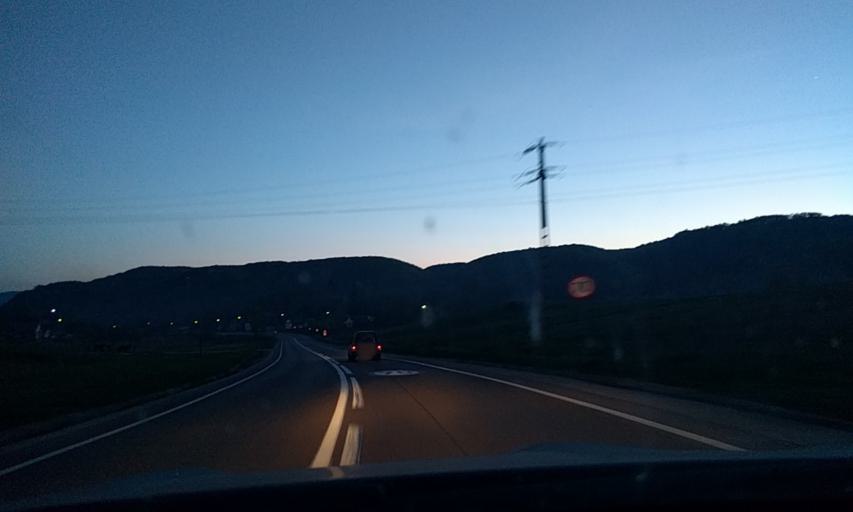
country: RO
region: Mures
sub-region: Comuna Saschiz
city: Saschiz
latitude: 46.2058
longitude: 24.9684
